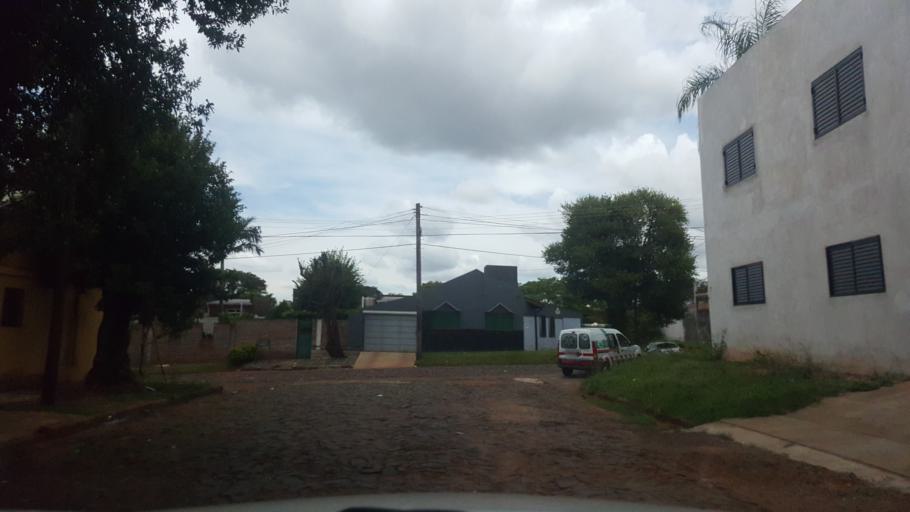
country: AR
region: Misiones
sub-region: Departamento de Capital
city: Posadas
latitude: -27.4008
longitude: -55.8972
